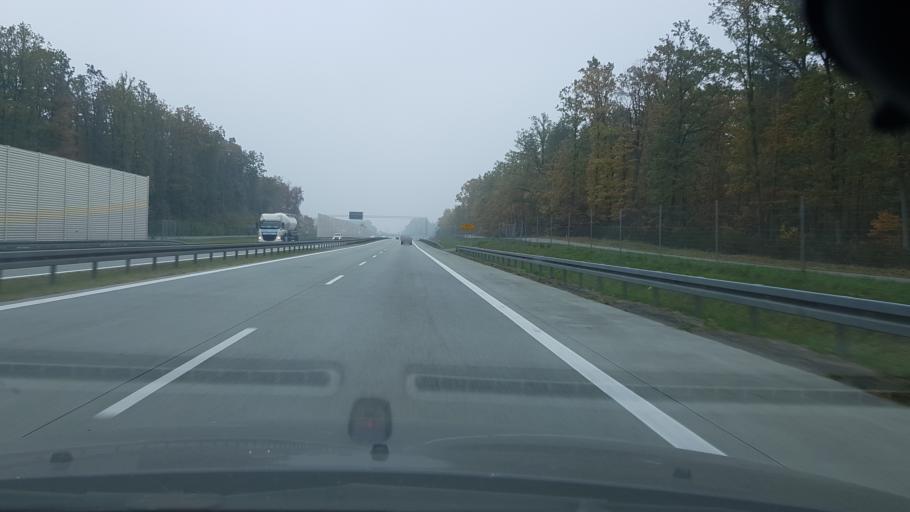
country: PL
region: Lodz Voivodeship
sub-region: Powiat rawski
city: Rawa Mazowiecka
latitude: 51.8085
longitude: 20.3060
